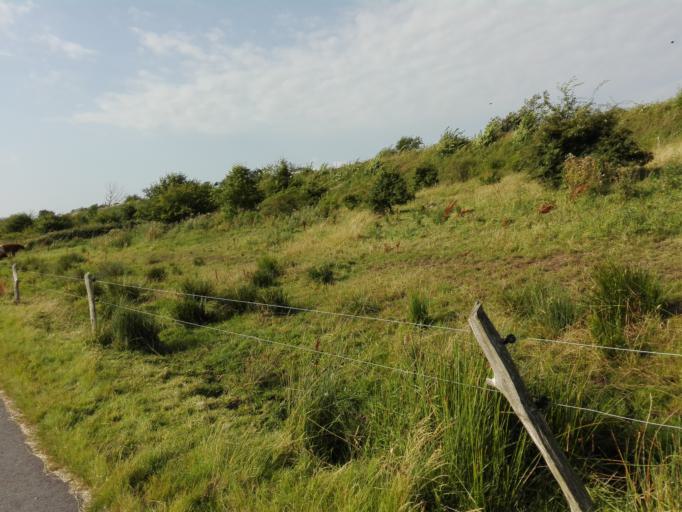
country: DK
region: Central Jutland
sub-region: Arhus Kommune
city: Lystrup
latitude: 56.2197
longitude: 10.2075
